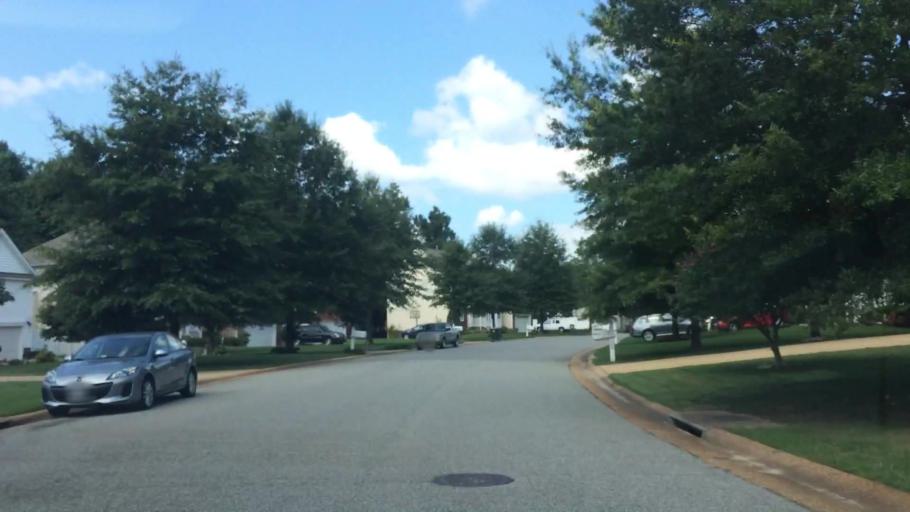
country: US
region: Virginia
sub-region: City of Williamsburg
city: Williamsburg
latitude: 37.2870
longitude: -76.6762
